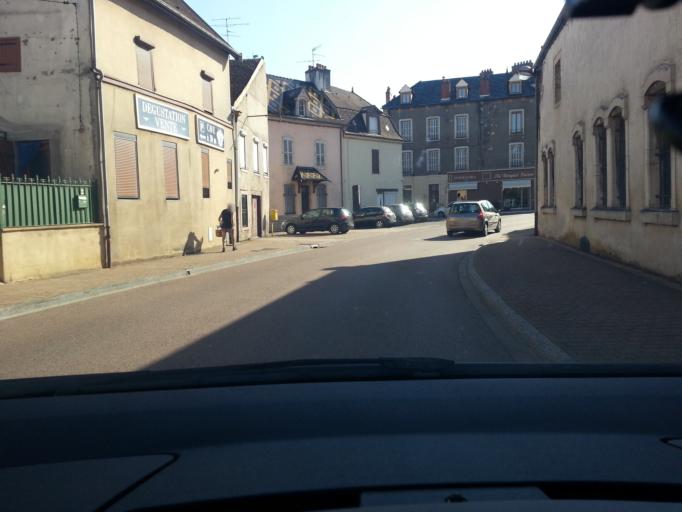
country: FR
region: Bourgogne
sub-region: Departement de la Cote-d'Or
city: Nuits-Saint-Georges
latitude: 47.1352
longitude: 4.9493
